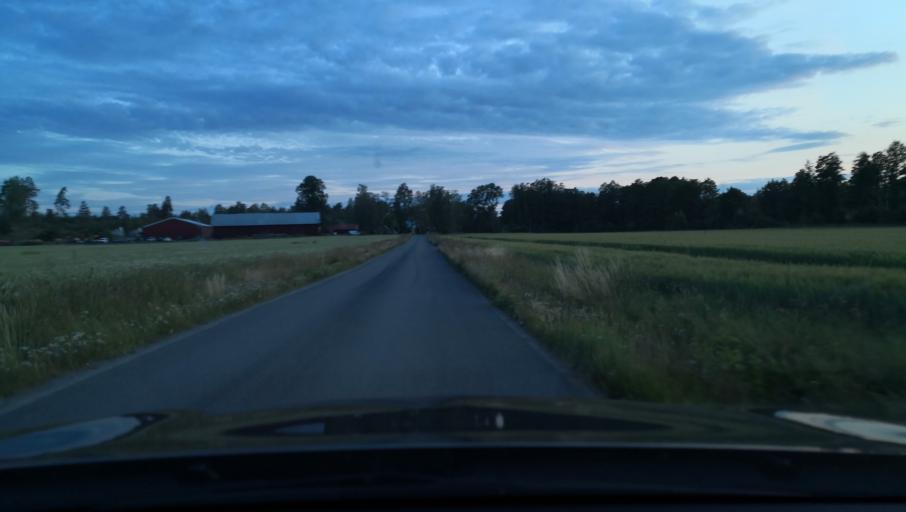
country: SE
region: Uppsala
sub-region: Osthammars Kommun
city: Bjorklinge
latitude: 60.0340
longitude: 17.4704
